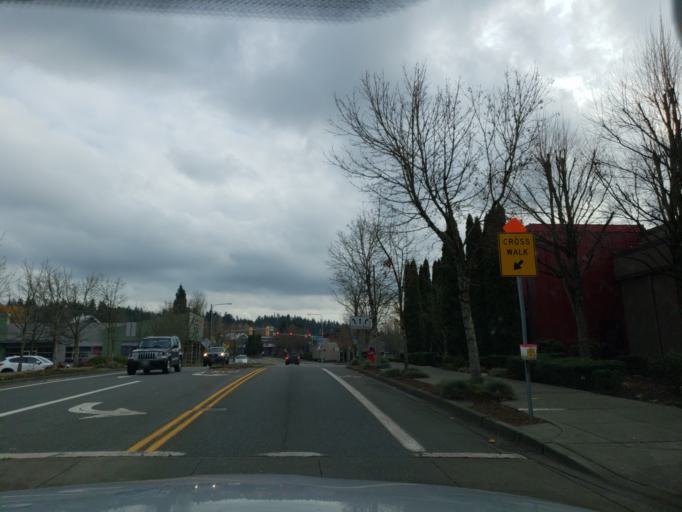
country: US
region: Washington
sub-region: King County
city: Woodinville
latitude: 47.7580
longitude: -122.1556
